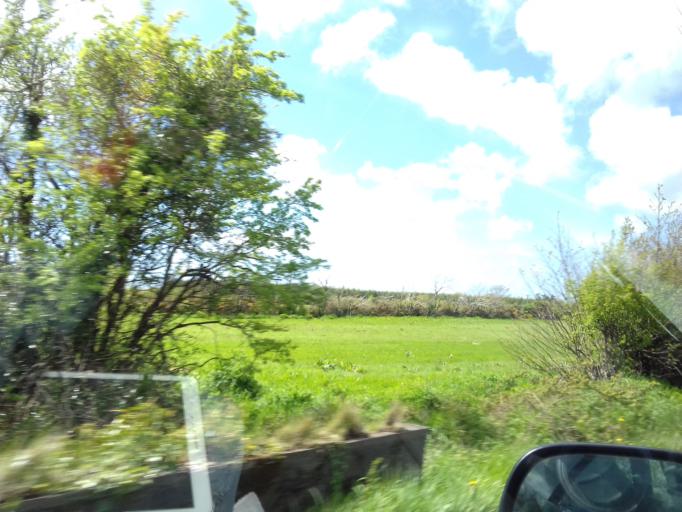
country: IE
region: Leinster
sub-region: Loch Garman
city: Loch Garman
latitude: 52.2837
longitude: -6.6448
